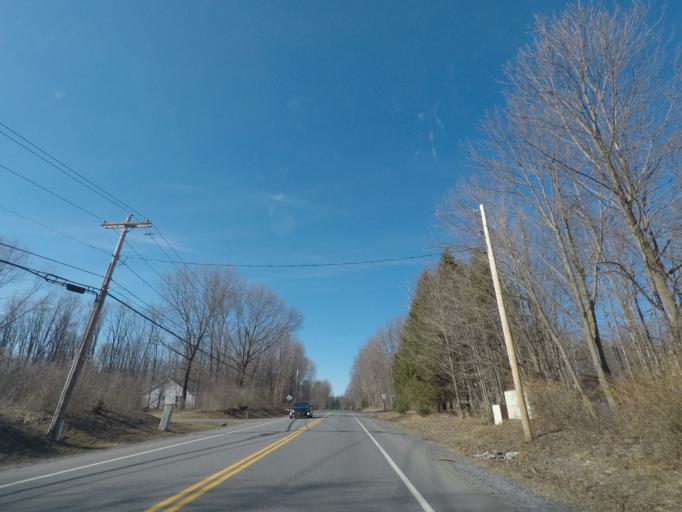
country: US
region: New York
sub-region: Saratoga County
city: Milton
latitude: 43.0705
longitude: -73.8477
